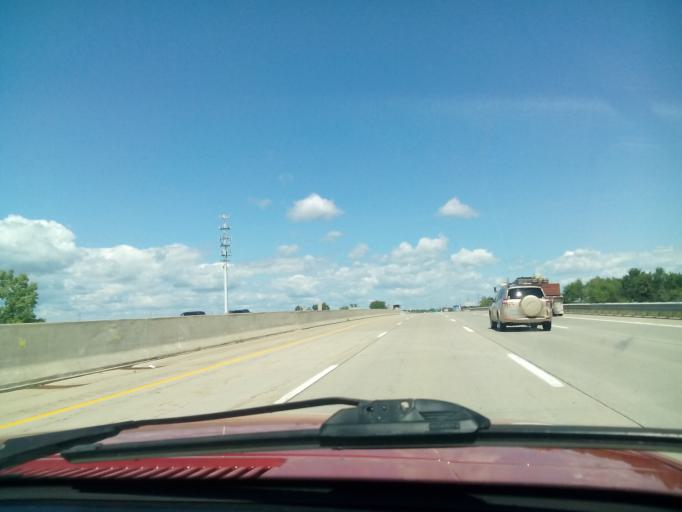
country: US
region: Michigan
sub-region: Bay County
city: Bay City
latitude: 43.6039
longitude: -83.9478
